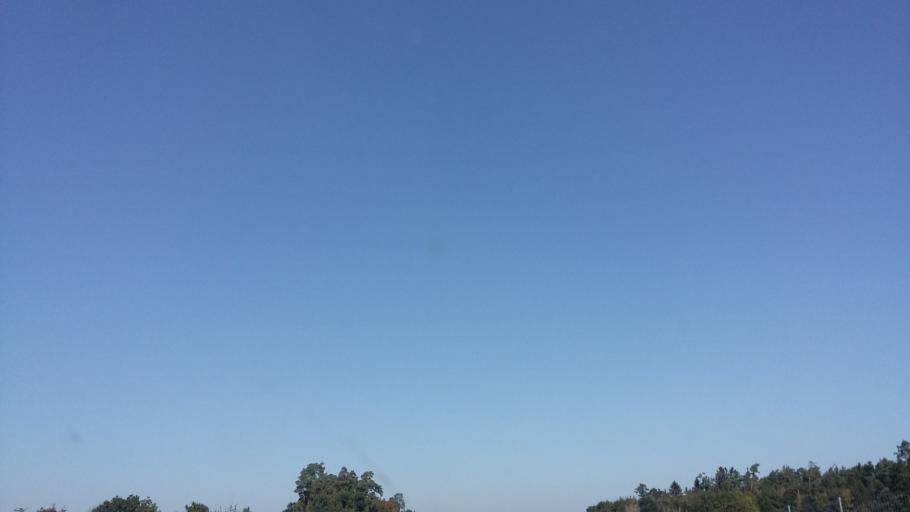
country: DE
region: Bavaria
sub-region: Upper Bavaria
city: Hurlach
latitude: 48.1006
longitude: 10.8370
